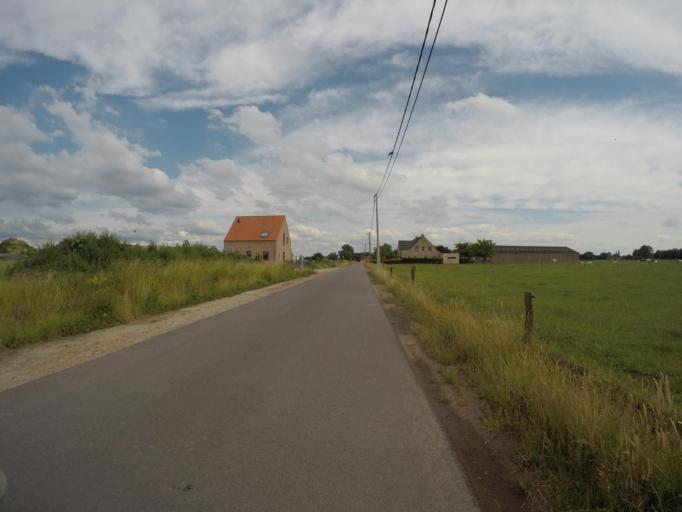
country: BE
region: Flanders
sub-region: Provincie Antwerpen
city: Rijkevorsel
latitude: 51.3684
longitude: 4.7487
